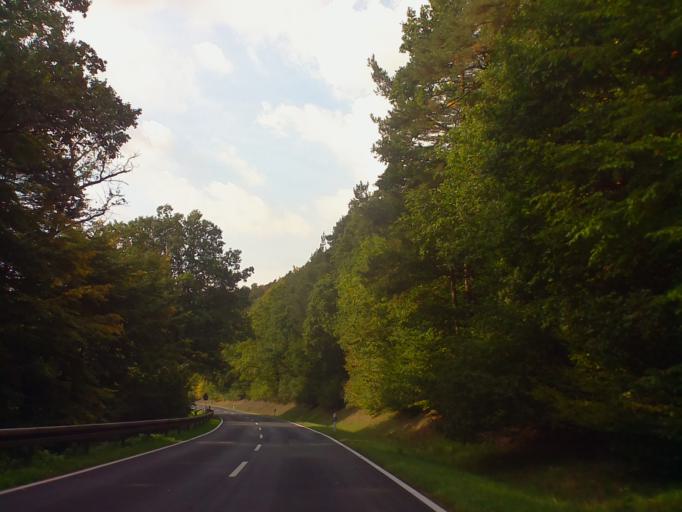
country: DE
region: Thuringia
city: Grossensee
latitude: 50.9486
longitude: 9.9770
